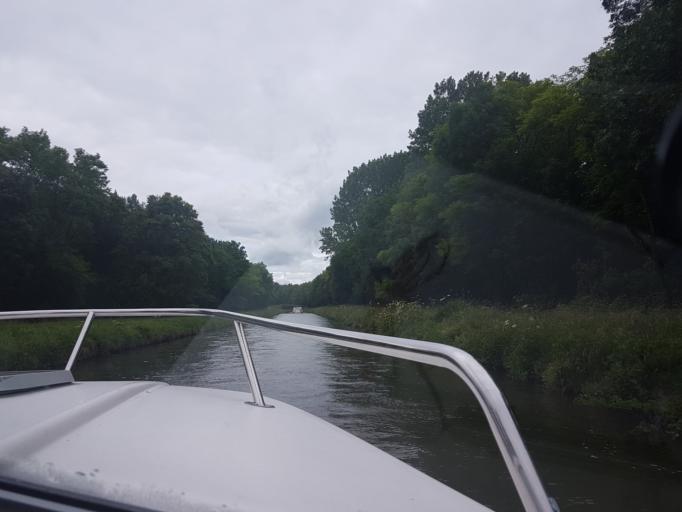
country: FR
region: Bourgogne
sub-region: Departement de l'Yonne
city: Vermenton
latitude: 47.6501
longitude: 3.6680
